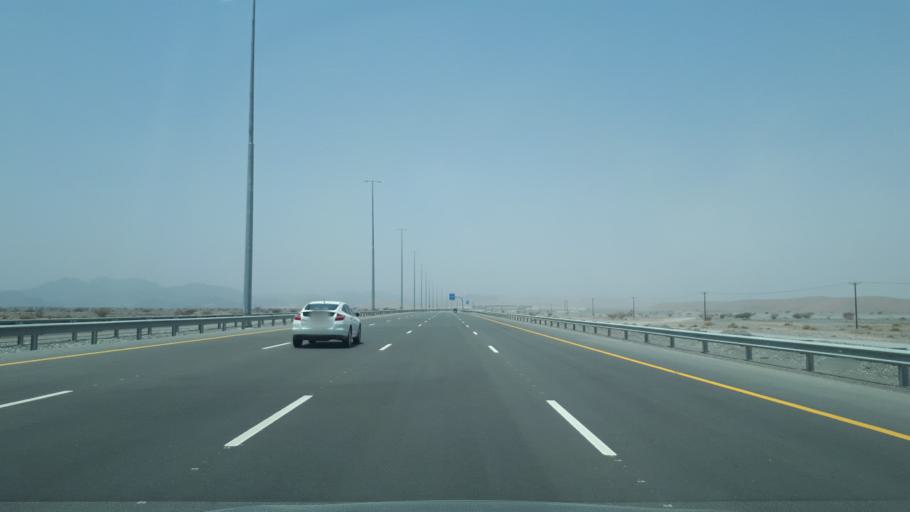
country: OM
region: Al Batinah
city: Barka'
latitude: 23.5379
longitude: 57.6746
